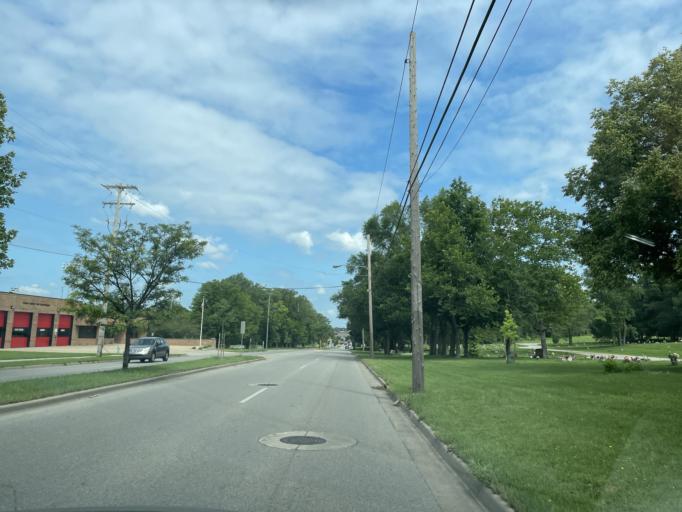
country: US
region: Michigan
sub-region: Kent County
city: East Grand Rapids
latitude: 42.9163
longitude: -85.6304
